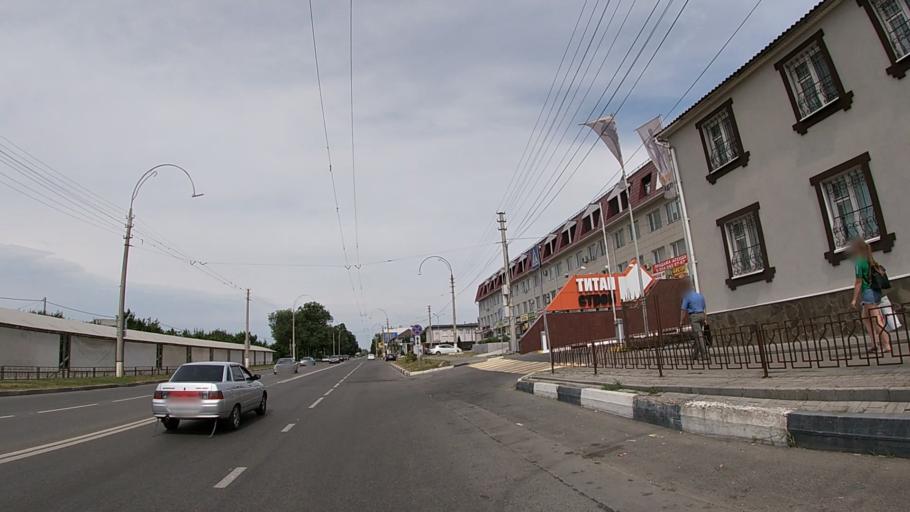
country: RU
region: Belgorod
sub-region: Belgorodskiy Rayon
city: Belgorod
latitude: 50.6029
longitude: 36.5606
